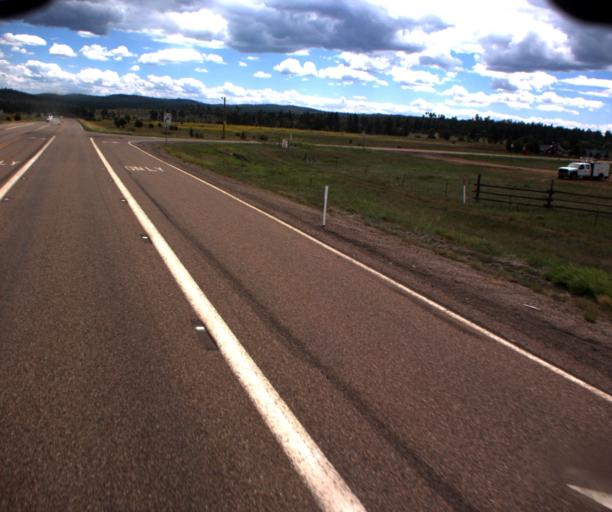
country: US
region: Arizona
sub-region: Navajo County
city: Linden
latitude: 34.3186
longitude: -110.2483
